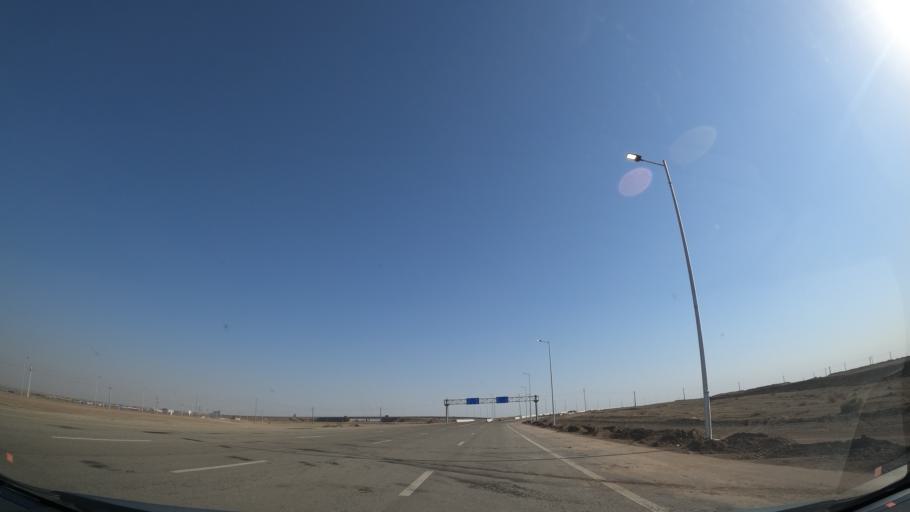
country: IR
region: Tehran
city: Eqbaliyeh
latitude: 35.1368
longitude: 51.5069
